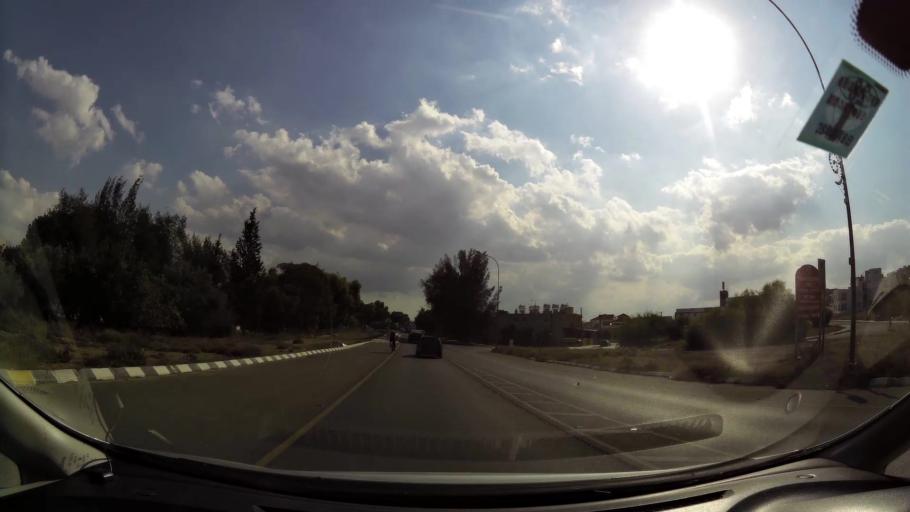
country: CY
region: Lefkosia
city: Nicosia
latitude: 35.1608
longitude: 33.3111
